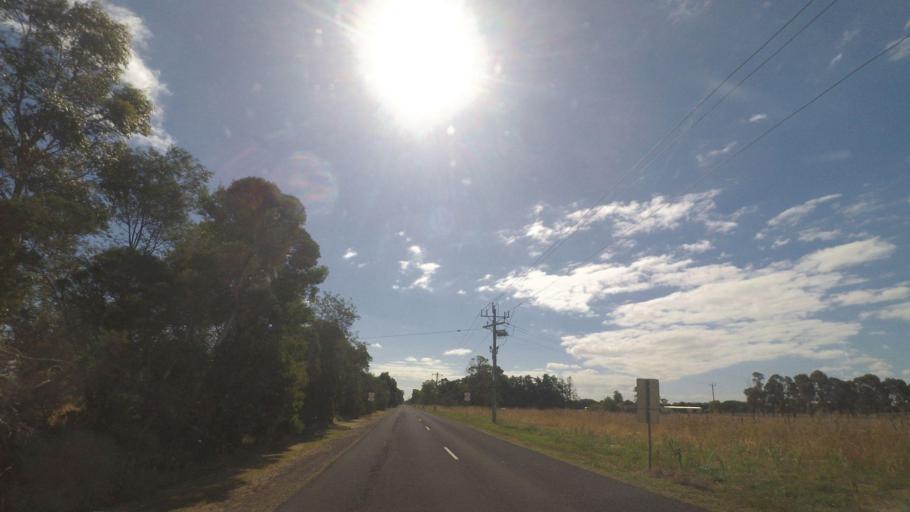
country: AU
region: Victoria
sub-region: Cardinia
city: Pakenham South
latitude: -38.1745
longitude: 145.5632
